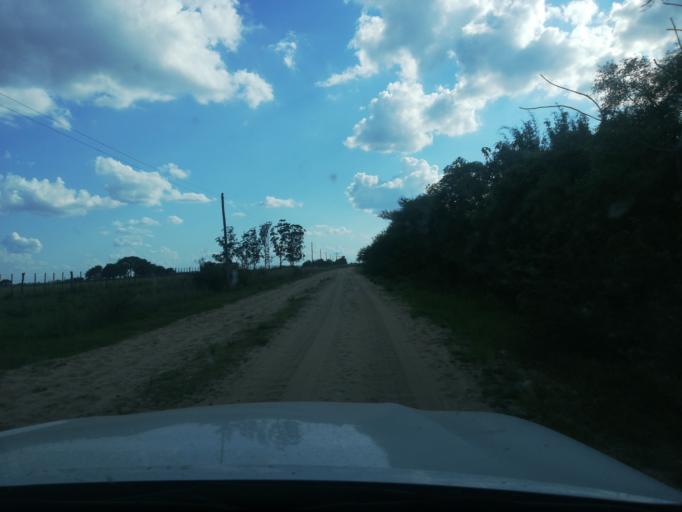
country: AR
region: Corrientes
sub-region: Departamento de San Miguel
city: San Miguel
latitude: -27.9956
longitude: -57.5785
